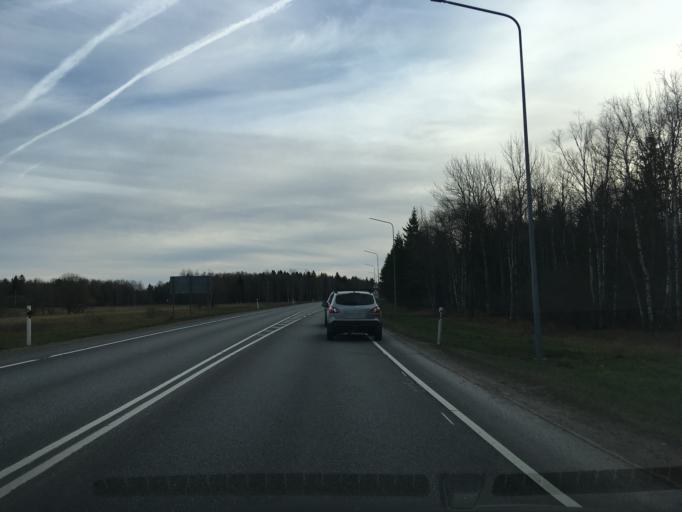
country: EE
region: Ida-Virumaa
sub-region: Kohtla-Jaerve linn
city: Kohtla-Jarve
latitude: 59.4199
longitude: 27.2805
